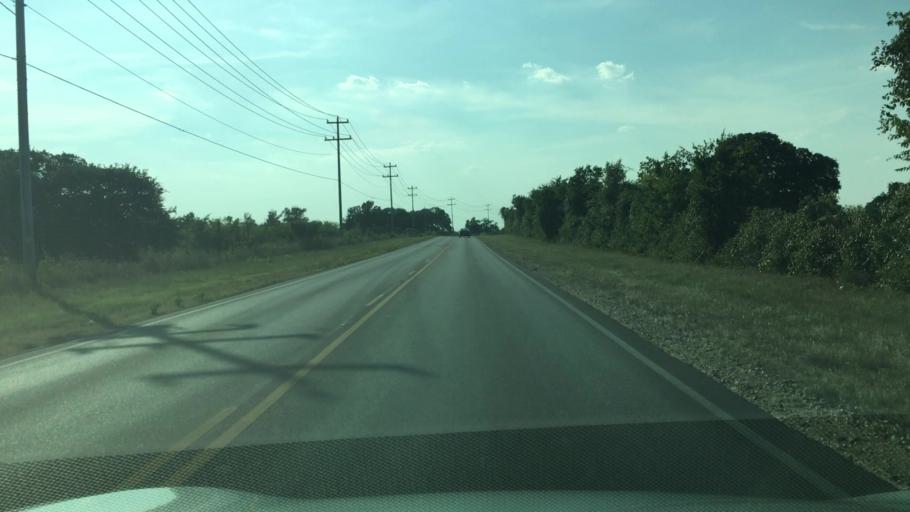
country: US
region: Texas
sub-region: Hays County
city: Buda
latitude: 30.0996
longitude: -97.9351
